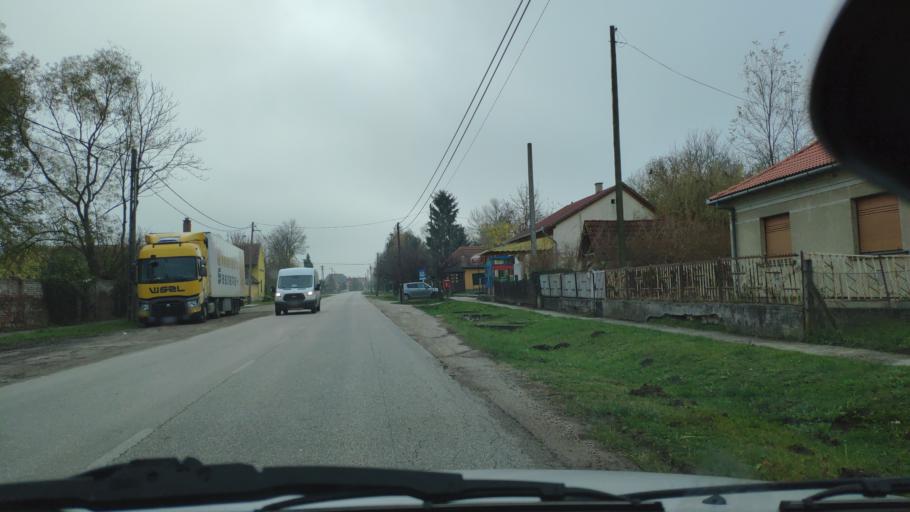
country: HU
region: Somogy
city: Balatonbereny
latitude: 46.6741
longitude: 17.2891
